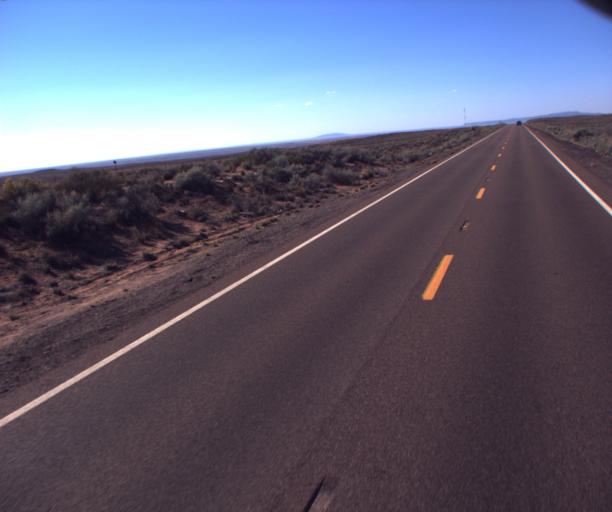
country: US
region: Arizona
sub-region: Navajo County
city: Winslow
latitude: 35.0421
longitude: -110.6078
